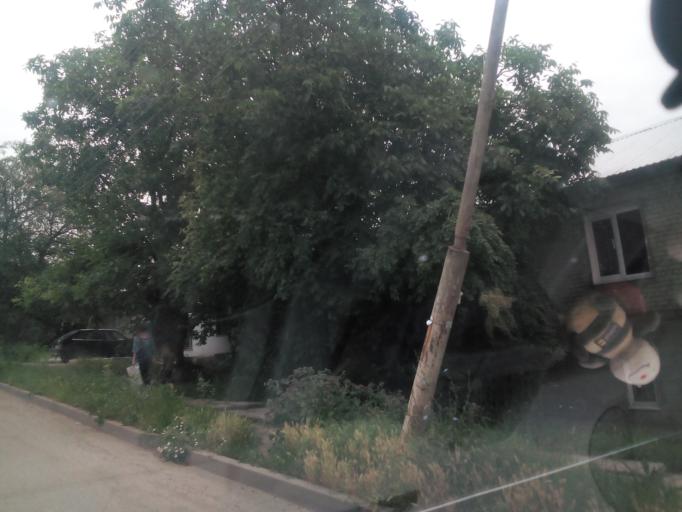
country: RU
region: Stavropol'skiy
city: Zheleznovodsk
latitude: 44.1494
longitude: 43.0044
